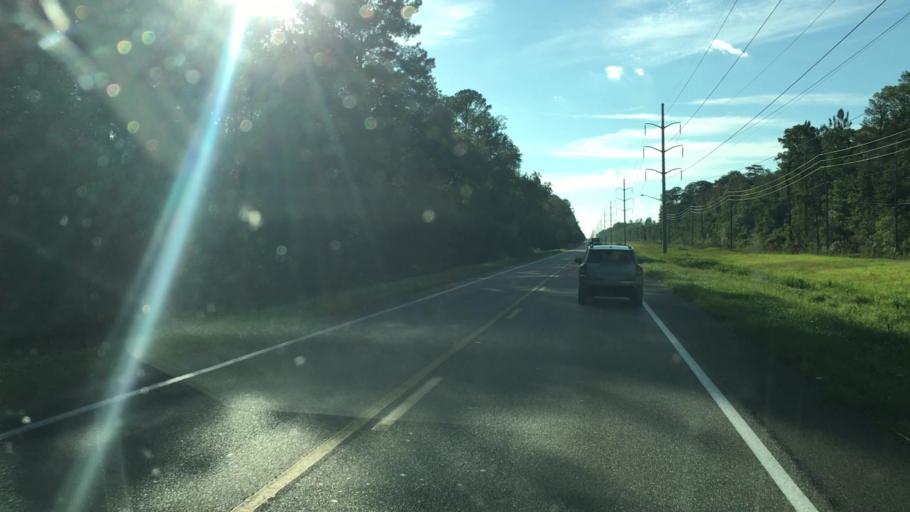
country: US
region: Florida
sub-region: Alachua County
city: Gainesville
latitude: 29.7031
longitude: -82.3198
